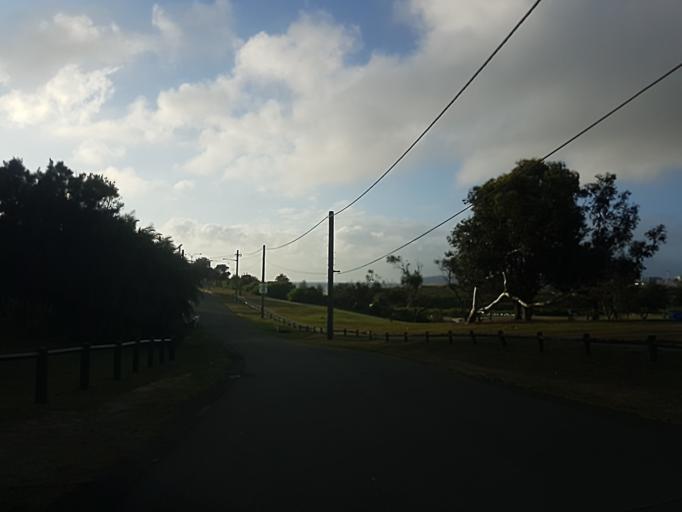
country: AU
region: New South Wales
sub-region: Warringah
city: North Curl Curl
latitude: -33.7632
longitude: 151.2967
